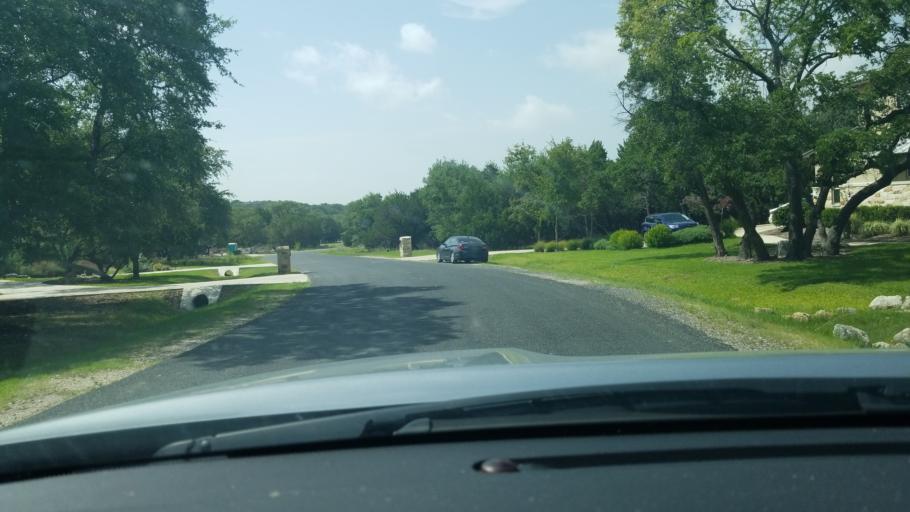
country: US
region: Texas
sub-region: Bexar County
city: Timberwood Park
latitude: 29.6985
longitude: -98.4920
